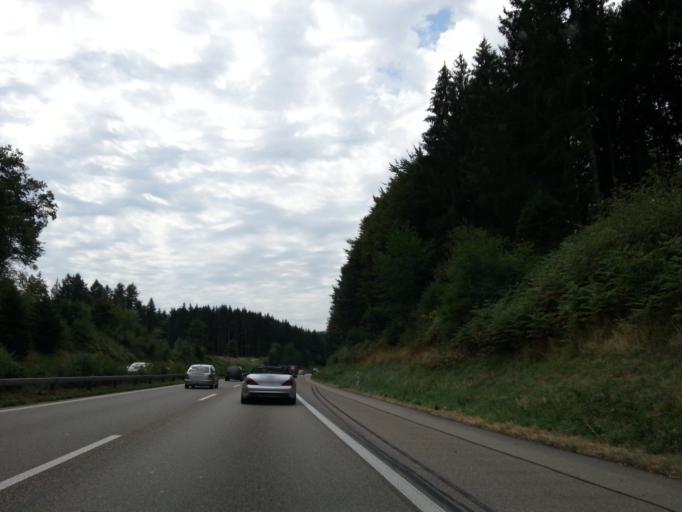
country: CH
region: Bern
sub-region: Bern-Mittelland District
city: Bariswil
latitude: 47.0325
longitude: 7.5277
